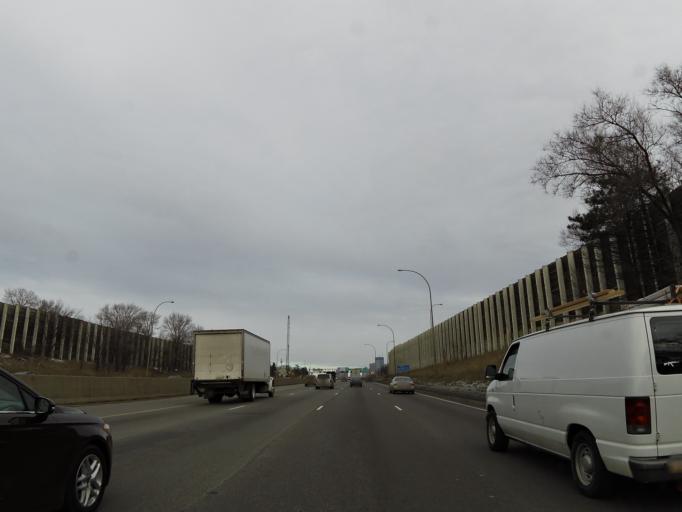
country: US
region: Minnesota
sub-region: Hennepin County
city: Minneapolis
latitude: 44.9398
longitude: -93.2745
